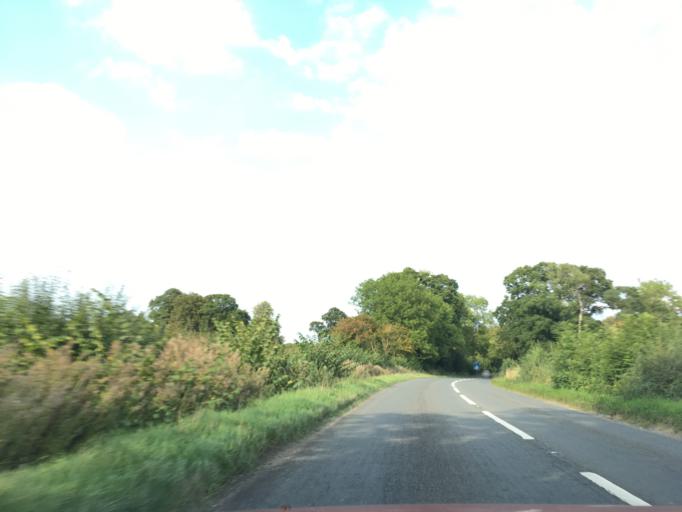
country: GB
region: England
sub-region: Gloucestershire
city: Tetbury
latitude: 51.6648
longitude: -2.1115
